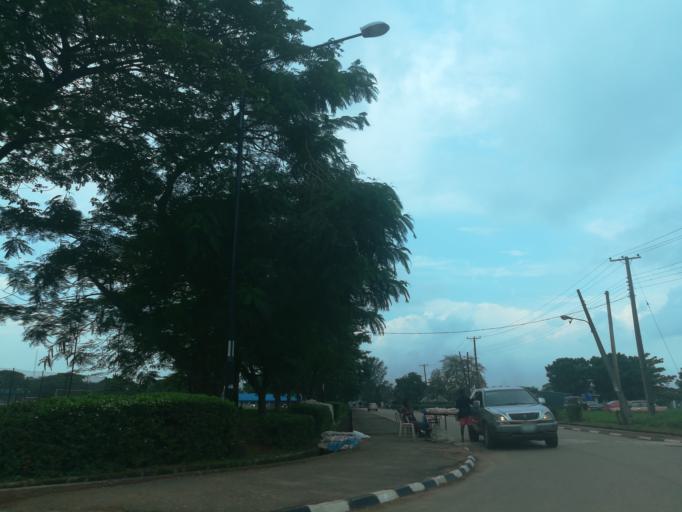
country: NG
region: Lagos
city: Ikorodu
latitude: 6.6456
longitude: 3.5203
